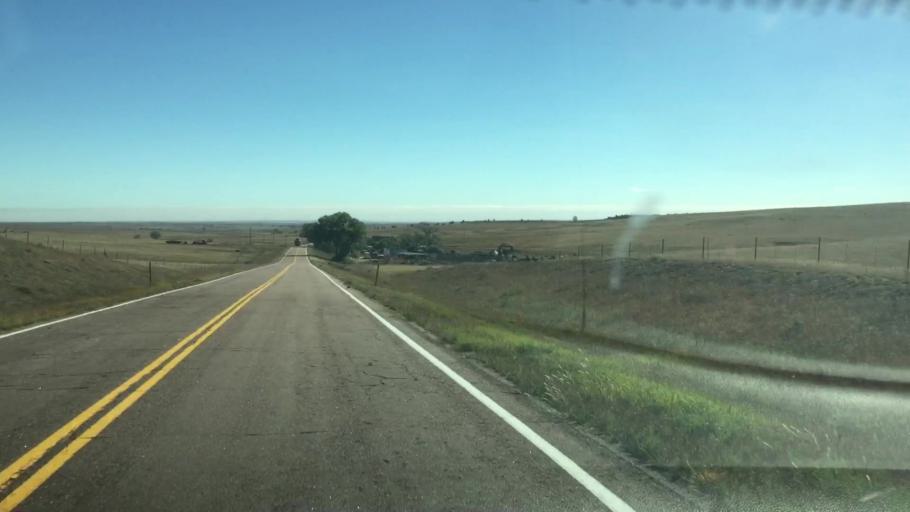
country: US
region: Colorado
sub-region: Lincoln County
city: Limon
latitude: 39.2882
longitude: -103.9650
